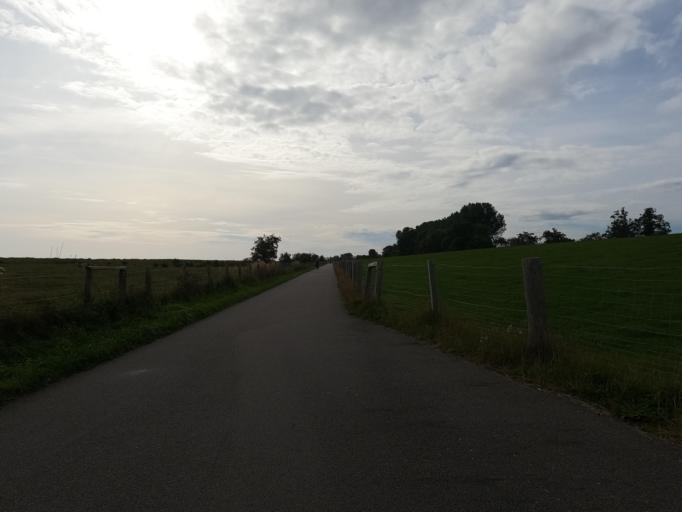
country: DE
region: Schleswig-Holstein
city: Dahme
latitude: 54.2507
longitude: 11.0800
